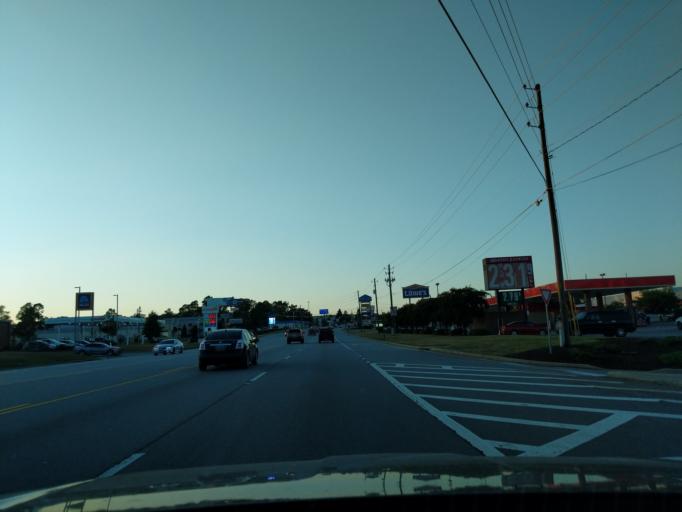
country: US
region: Georgia
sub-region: Columbia County
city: Martinez
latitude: 33.5063
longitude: -82.0914
